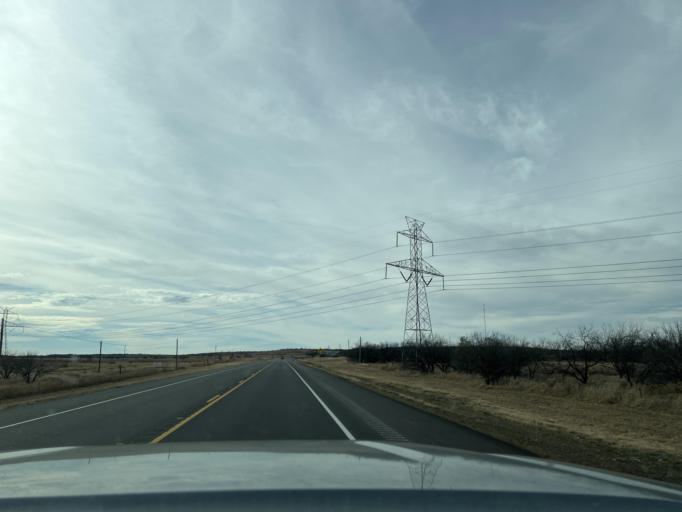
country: US
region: Texas
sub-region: Shackelford County
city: Albany
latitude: 32.7053
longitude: -99.4024
